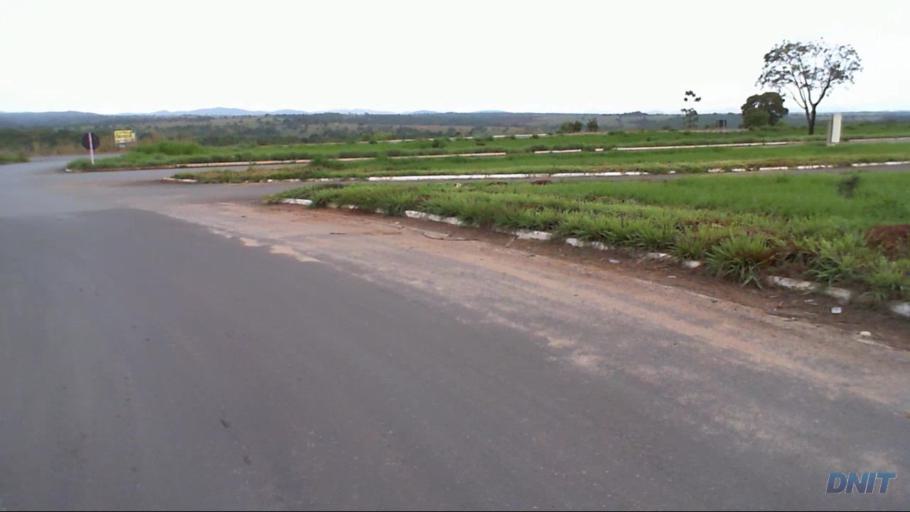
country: BR
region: Goias
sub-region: Uruacu
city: Uruacu
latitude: -14.6364
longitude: -49.1760
